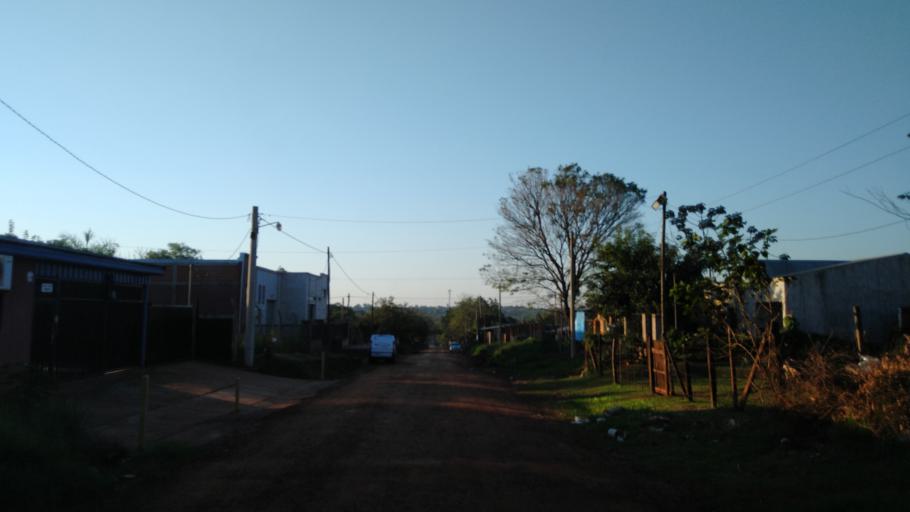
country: AR
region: Misiones
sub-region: Departamento de Capital
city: Posadas
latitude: -27.4253
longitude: -55.9210
